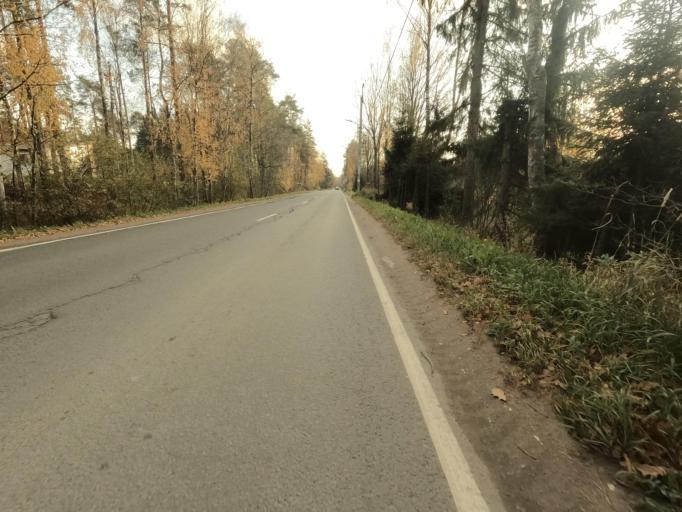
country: RU
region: St.-Petersburg
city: Beloostrov
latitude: 60.1638
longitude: 30.0082
